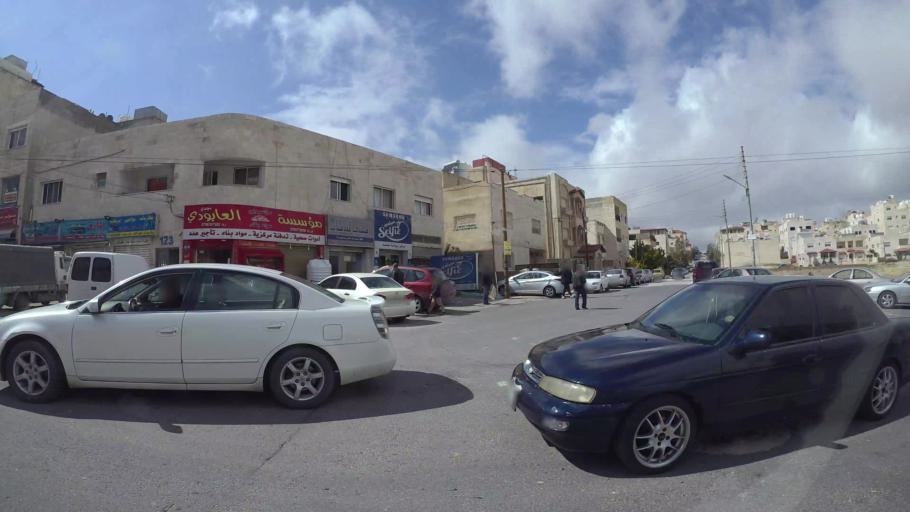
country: JO
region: Amman
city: Al Jubayhah
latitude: 32.0609
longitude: 35.8777
